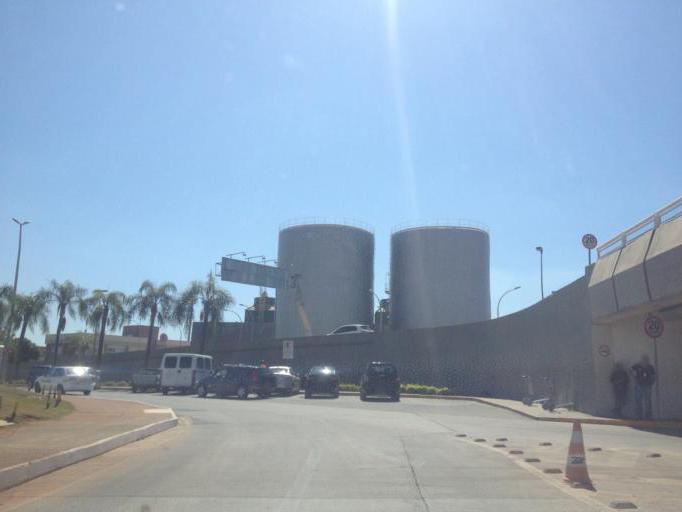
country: BR
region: Federal District
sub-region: Brasilia
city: Brasilia
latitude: -15.8692
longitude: -47.9218
